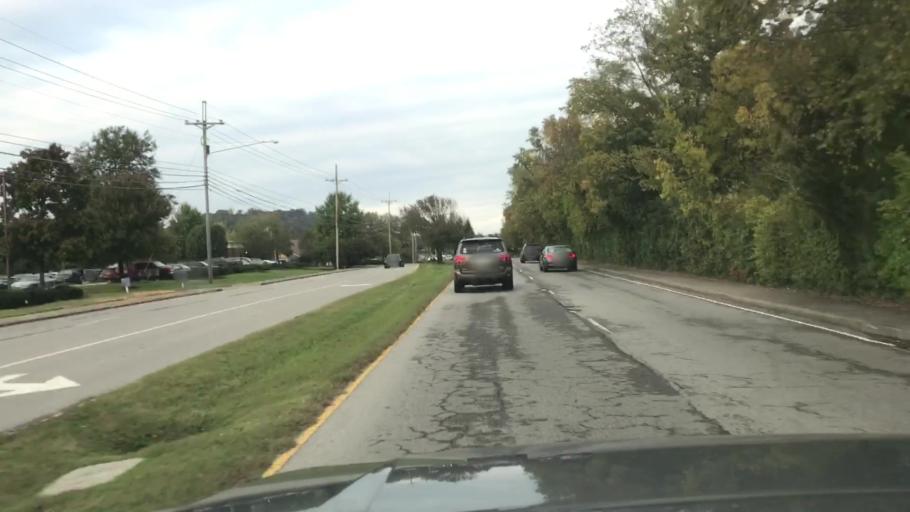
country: US
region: Tennessee
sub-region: Williamson County
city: Franklin
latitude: 35.9622
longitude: -86.8151
